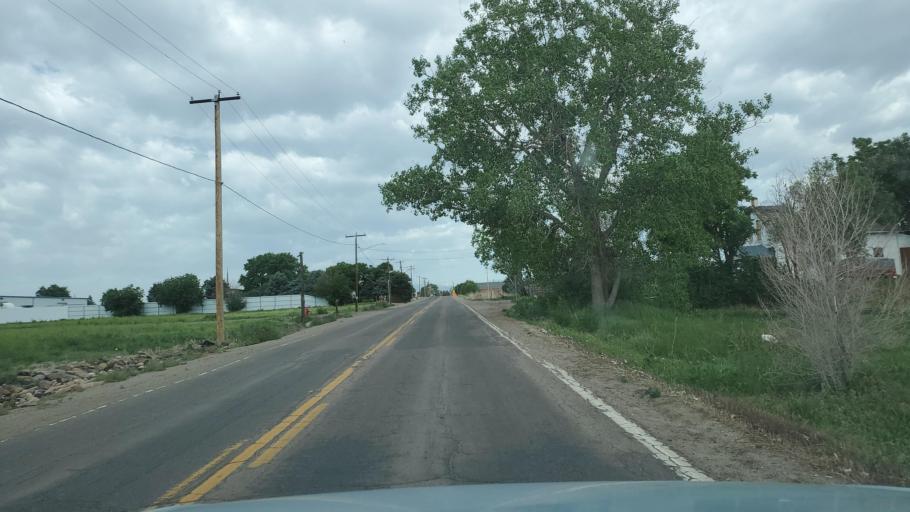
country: US
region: Colorado
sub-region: Adams County
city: Welby
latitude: 39.8381
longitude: -104.9517
